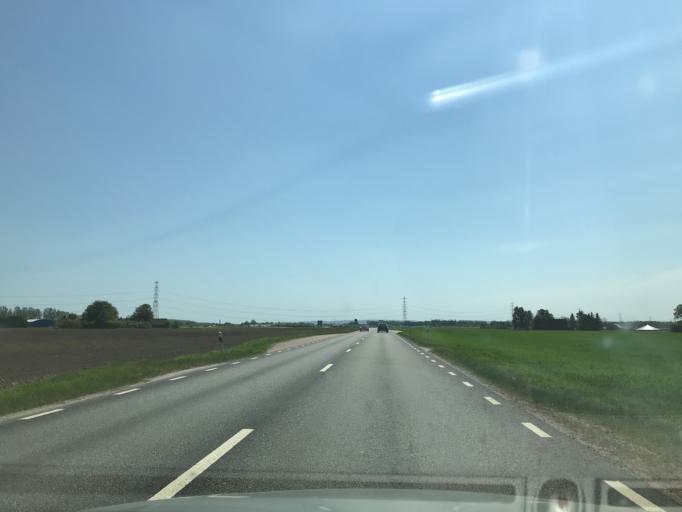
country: SE
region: Skane
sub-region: Astorps Kommun
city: Kvidinge
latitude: 56.2002
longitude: 13.0461
